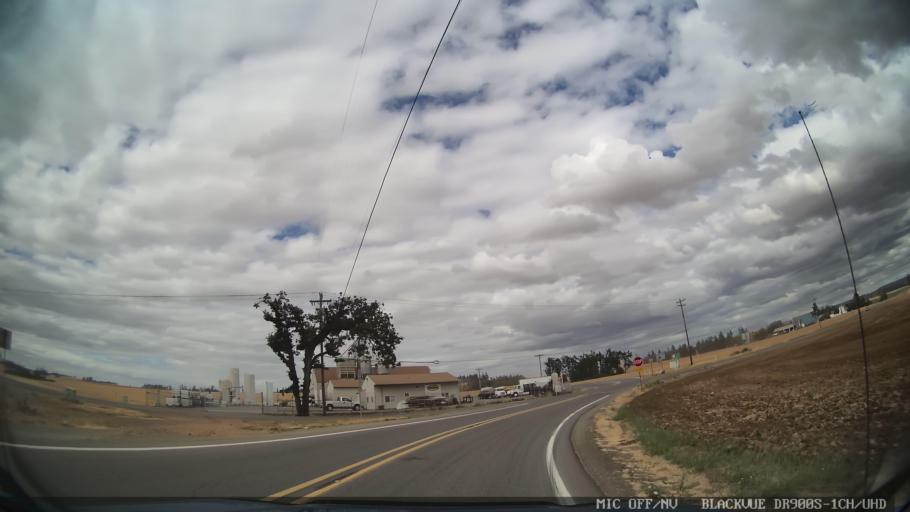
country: US
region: Oregon
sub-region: Marion County
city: Sublimity
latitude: 44.8659
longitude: -122.7923
